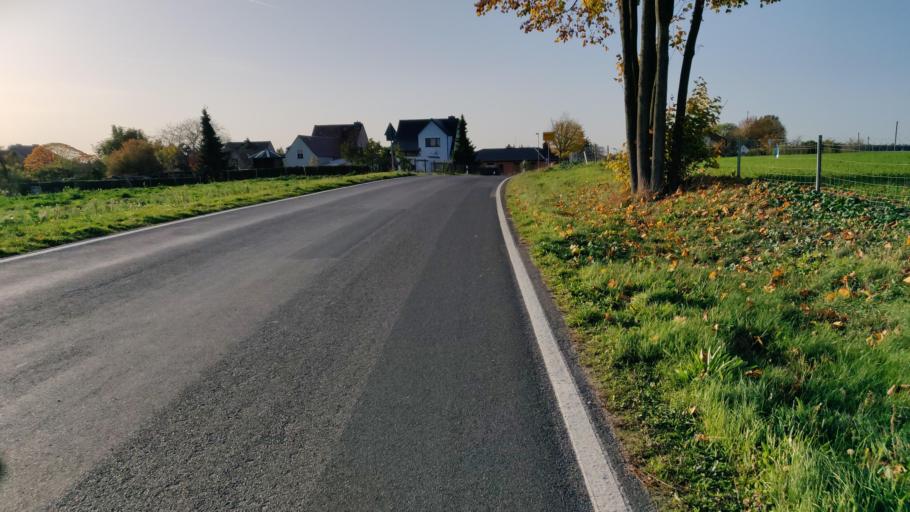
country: DE
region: Brandenburg
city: Grosskmehlen
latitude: 51.3544
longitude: 13.6980
